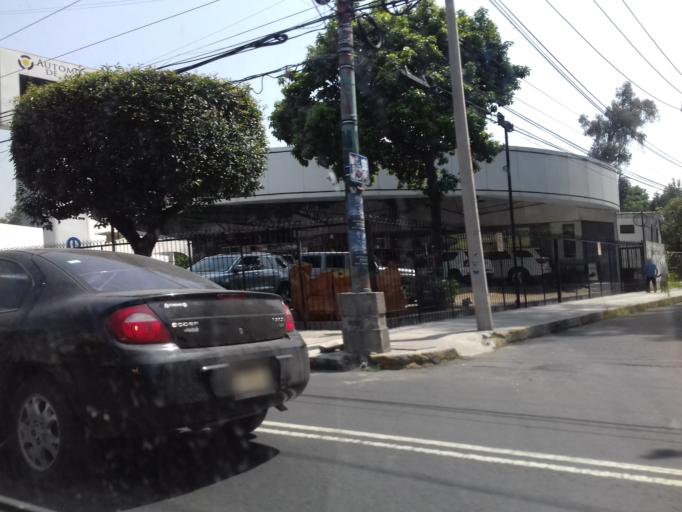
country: MX
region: Mexico City
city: Coyoacan
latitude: 19.3571
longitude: -99.1727
